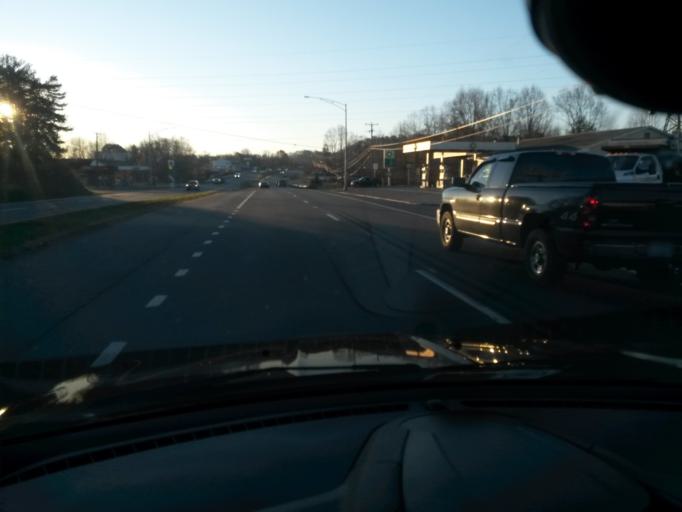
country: US
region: Virginia
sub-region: Franklin County
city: Rocky Mount
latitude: 37.0457
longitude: -79.8783
